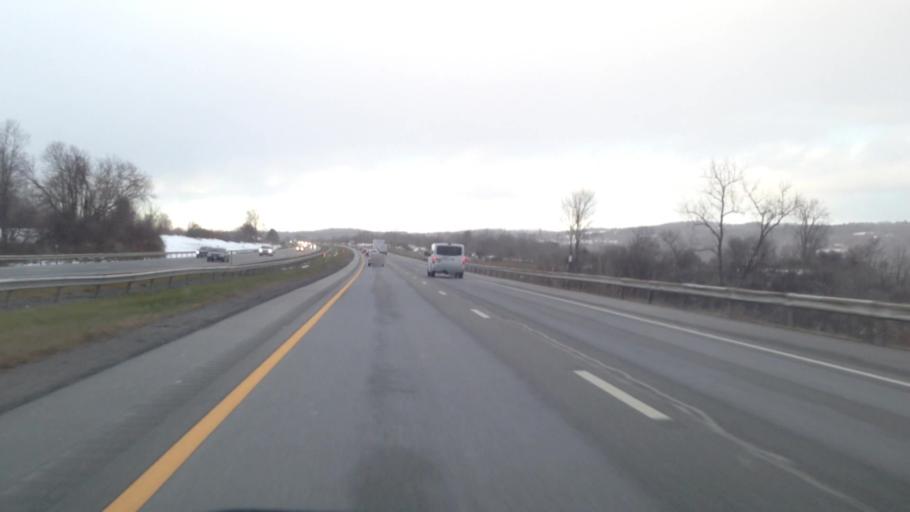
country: US
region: New York
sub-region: Montgomery County
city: Saint Johnsville
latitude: 42.9752
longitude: -74.6515
